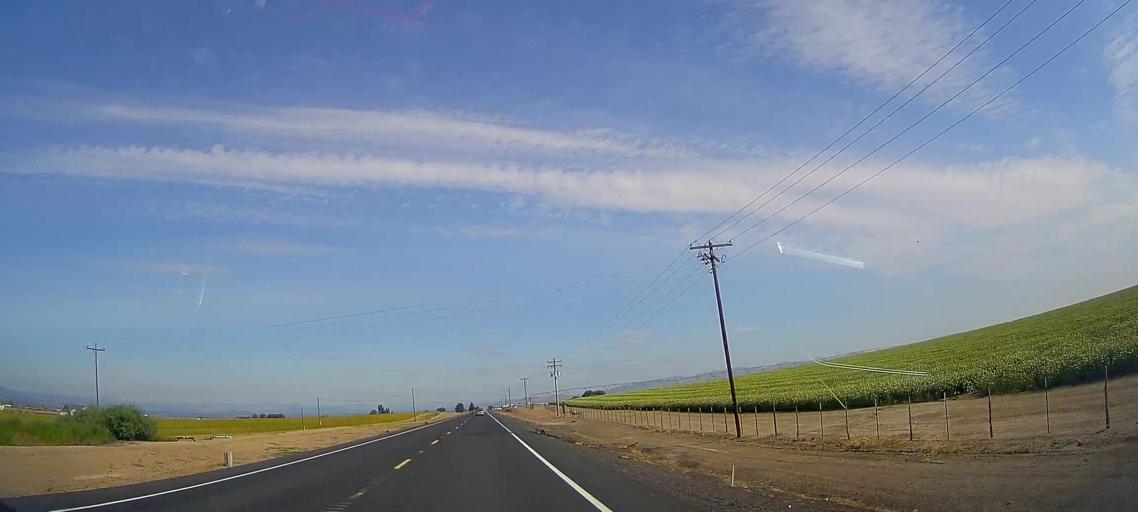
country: US
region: Oregon
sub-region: Jefferson County
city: Madras
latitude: 44.6826
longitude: -121.1488
